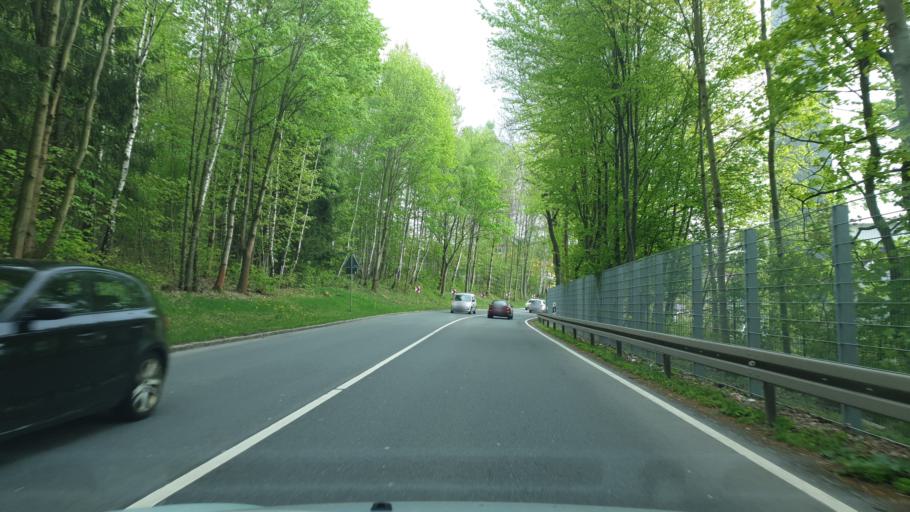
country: DE
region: Saxony
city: Aue
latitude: 50.5979
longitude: 12.7130
